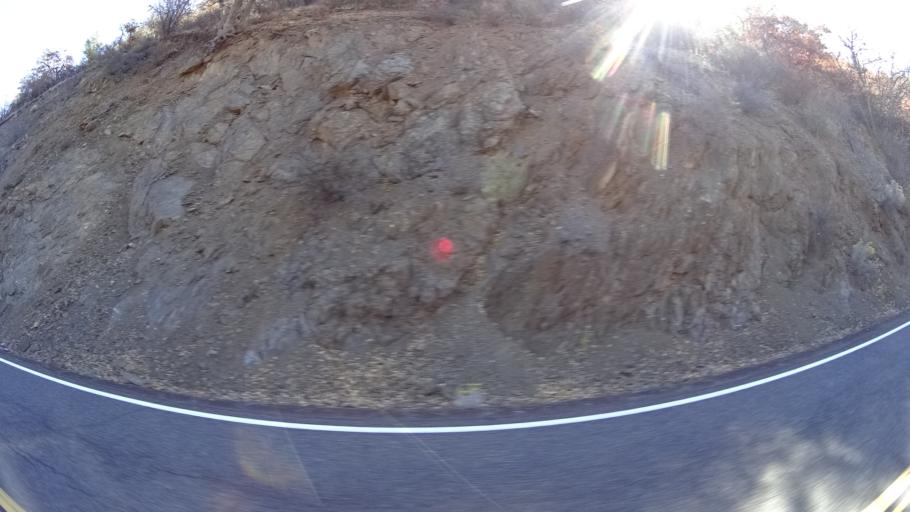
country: US
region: California
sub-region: Siskiyou County
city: Weed
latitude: 41.4711
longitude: -122.5897
